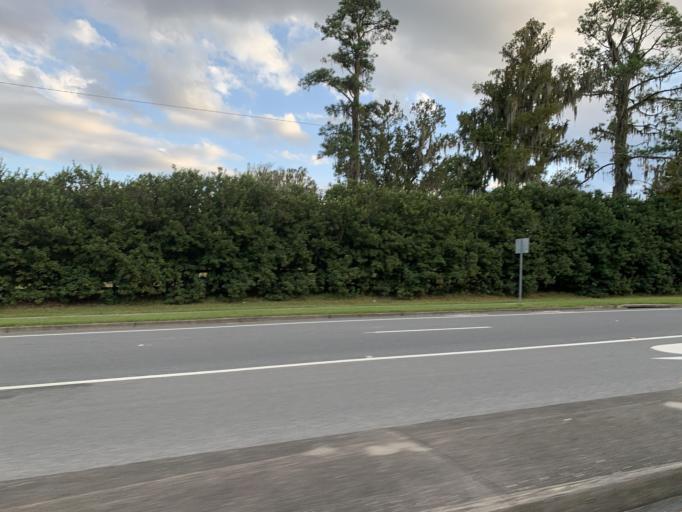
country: US
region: Florida
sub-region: Marion County
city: Ocala
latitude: 29.1515
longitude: -82.1541
